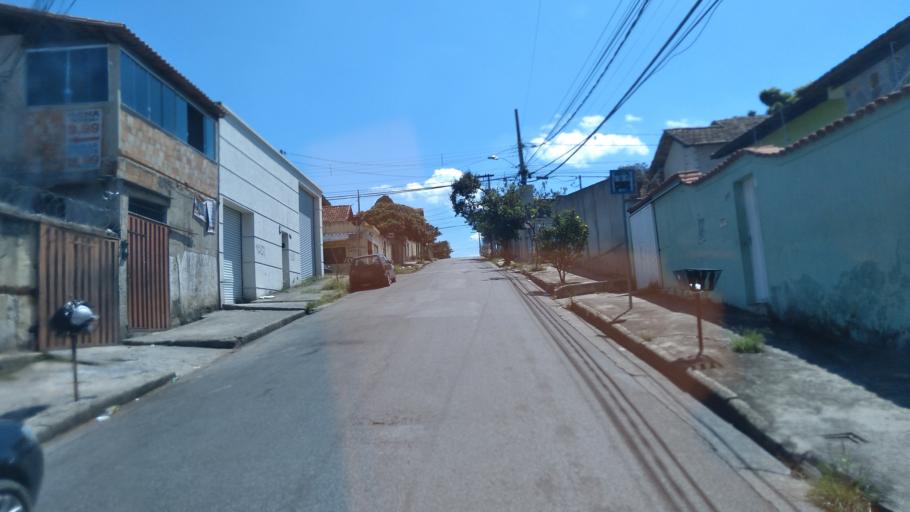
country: BR
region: Minas Gerais
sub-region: Belo Horizonte
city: Belo Horizonte
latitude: -19.8689
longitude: -43.9248
